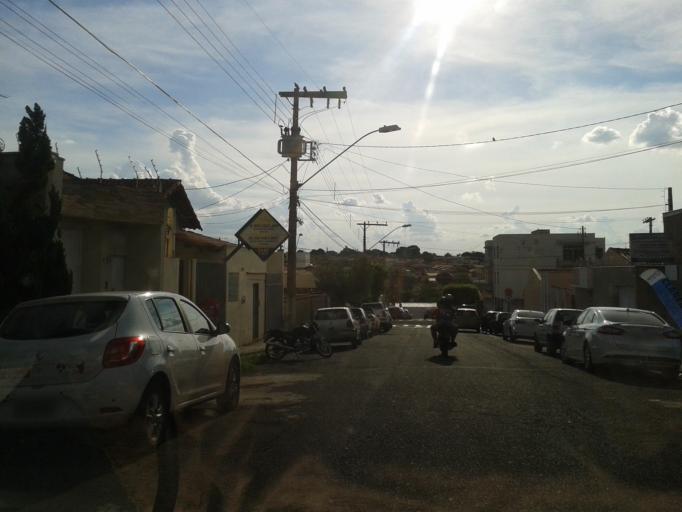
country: BR
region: Minas Gerais
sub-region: Ituiutaba
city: Ituiutaba
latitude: -18.9712
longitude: -49.4660
